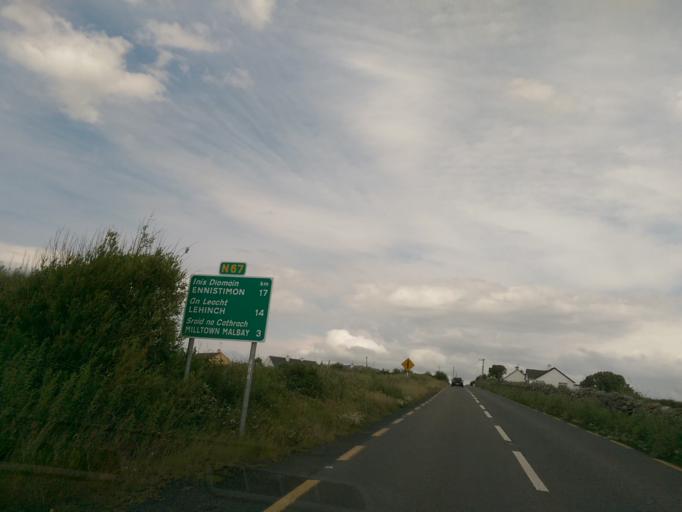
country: IE
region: Munster
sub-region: An Clar
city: Kilrush
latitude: 52.8453
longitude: -9.4201
